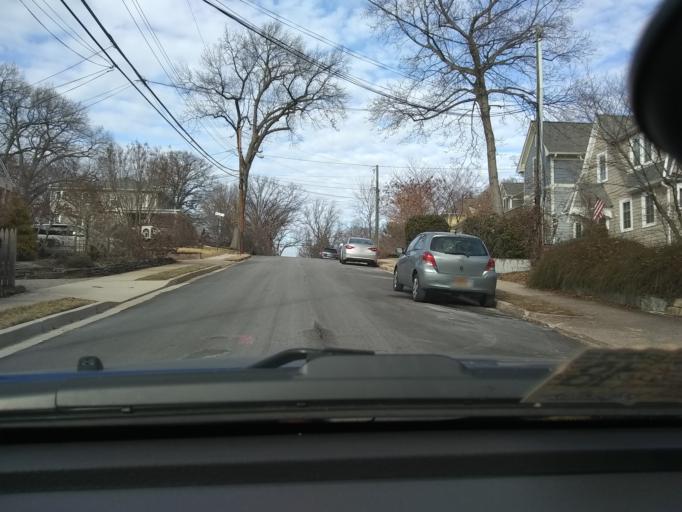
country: US
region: Virginia
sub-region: Arlington County
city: Arlington
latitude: 38.8911
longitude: -77.1130
